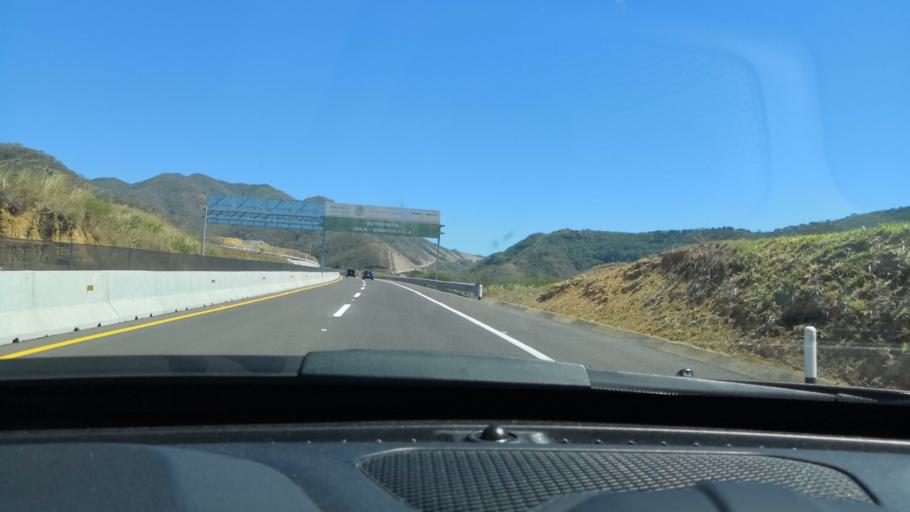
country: MX
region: Nayarit
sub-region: Compostela
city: Juan Escutia (Borbollon)
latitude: 21.1377
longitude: -104.9193
